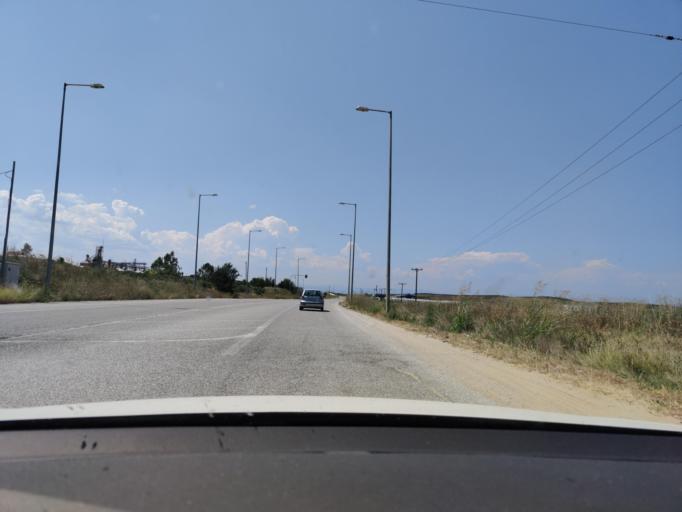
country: GR
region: Central Macedonia
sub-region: Nomos Serron
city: Draviskos
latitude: 40.9336
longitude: 23.8720
